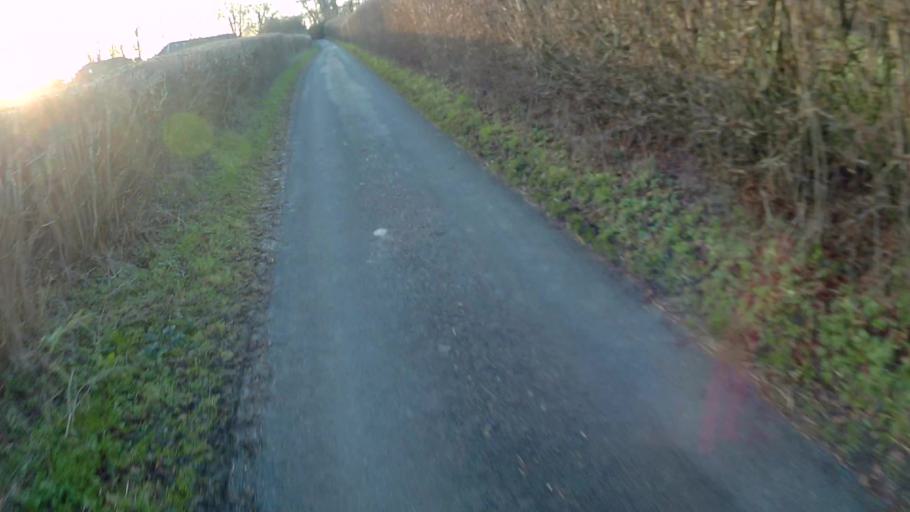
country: GB
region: England
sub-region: Hampshire
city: Basingstoke
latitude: 51.2125
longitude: -1.1429
